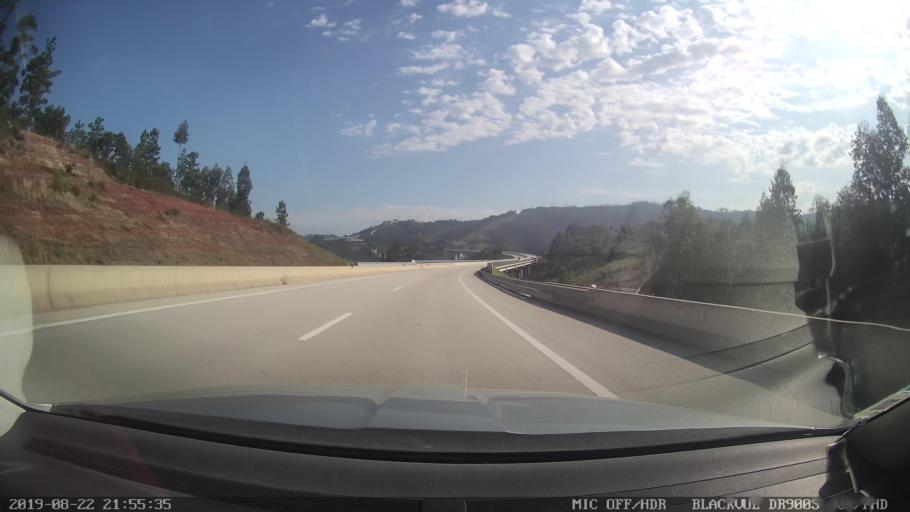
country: PT
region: Coimbra
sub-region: Coimbra
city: Coimbra
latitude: 40.1552
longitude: -8.3843
